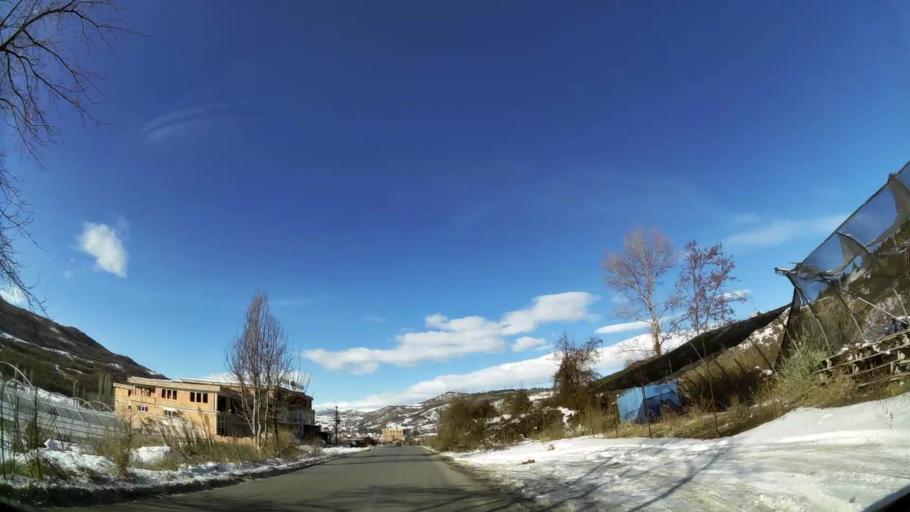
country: MK
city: Ljubin
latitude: 41.9868
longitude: 21.2999
